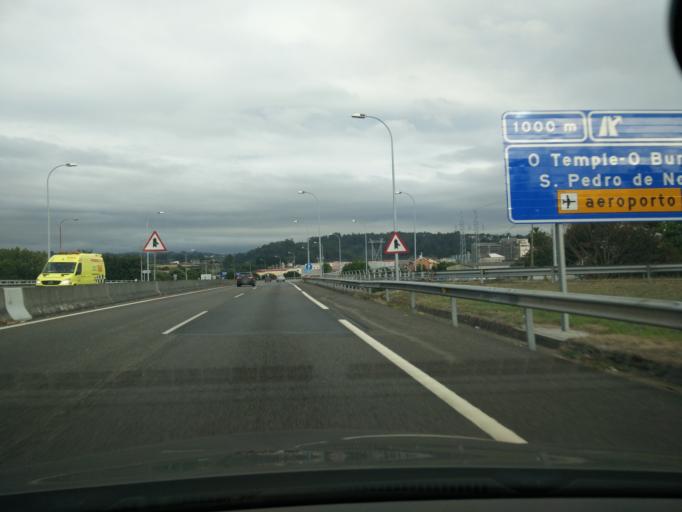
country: ES
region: Galicia
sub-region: Provincia da Coruna
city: Cambre
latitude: 43.3131
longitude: -8.3654
